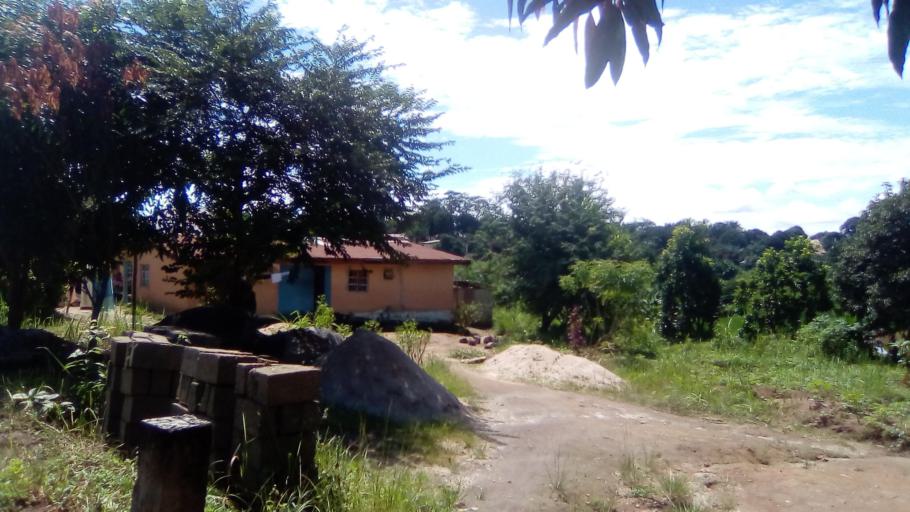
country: SL
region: Eastern Province
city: Koidu
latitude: 8.6357
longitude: -10.9942
